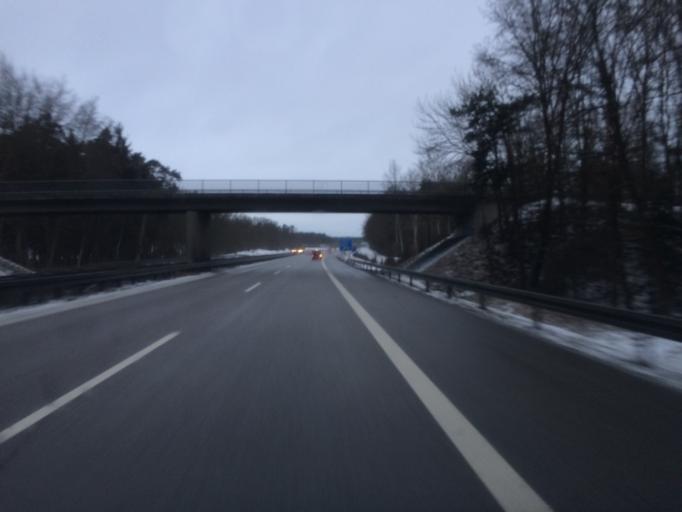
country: DE
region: Bavaria
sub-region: Upper Palatinate
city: Wackersdorf
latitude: 49.3361
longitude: 12.1507
